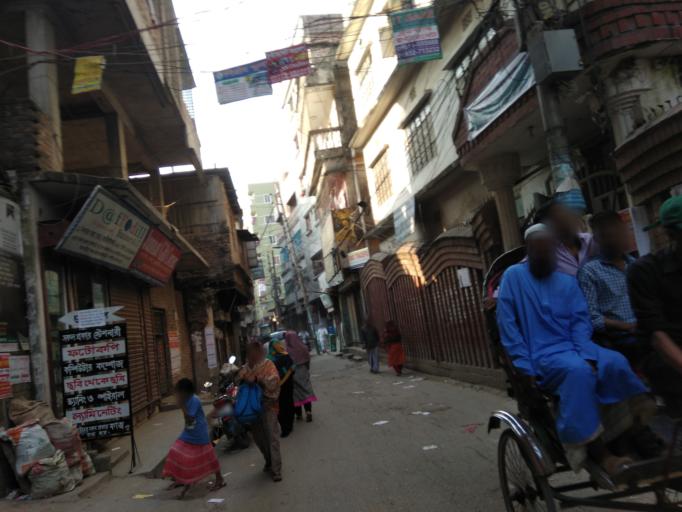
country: BD
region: Dhaka
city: Azimpur
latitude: 23.7253
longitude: 90.3747
